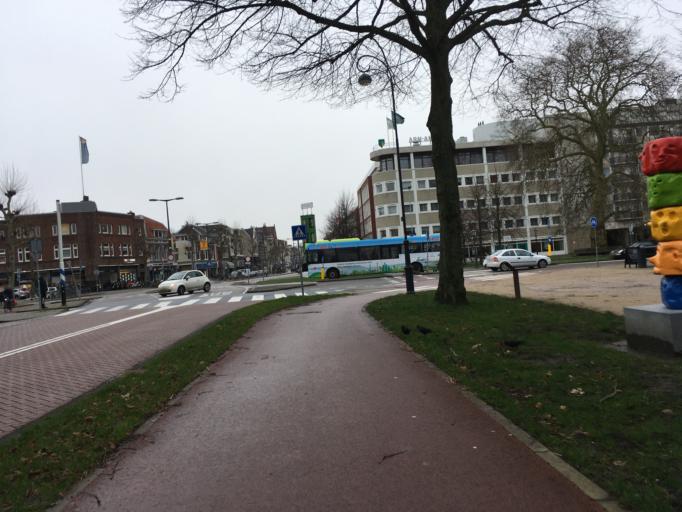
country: NL
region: North Holland
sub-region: Gemeente Haarlem
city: Haarlem
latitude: 52.3739
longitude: 4.6302
